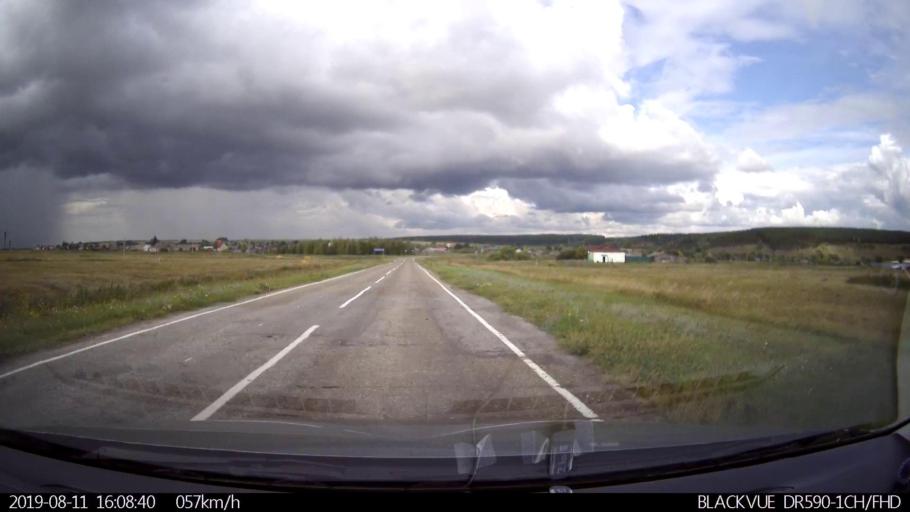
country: RU
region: Ulyanovsk
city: Ignatovka
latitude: 53.9866
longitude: 47.6488
